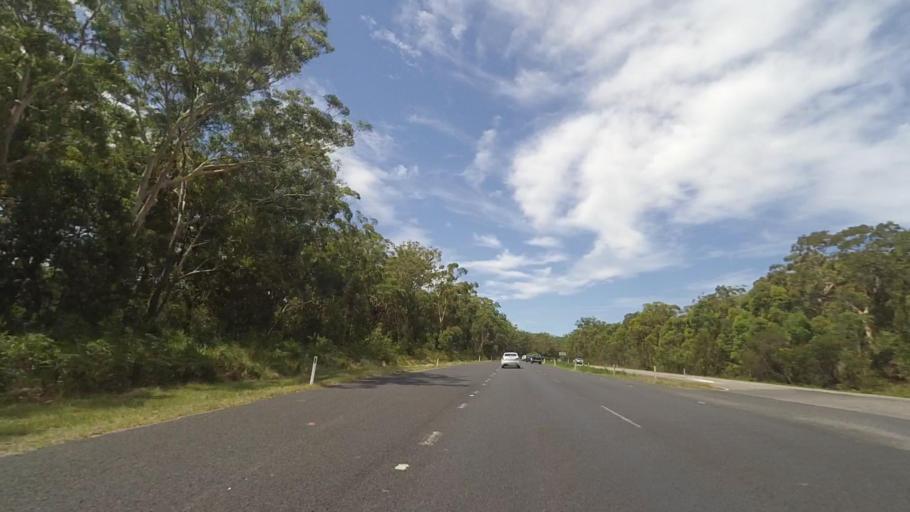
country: AU
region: New South Wales
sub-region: Port Stephens Shire
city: Anna Bay
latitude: -32.7759
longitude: 152.0048
